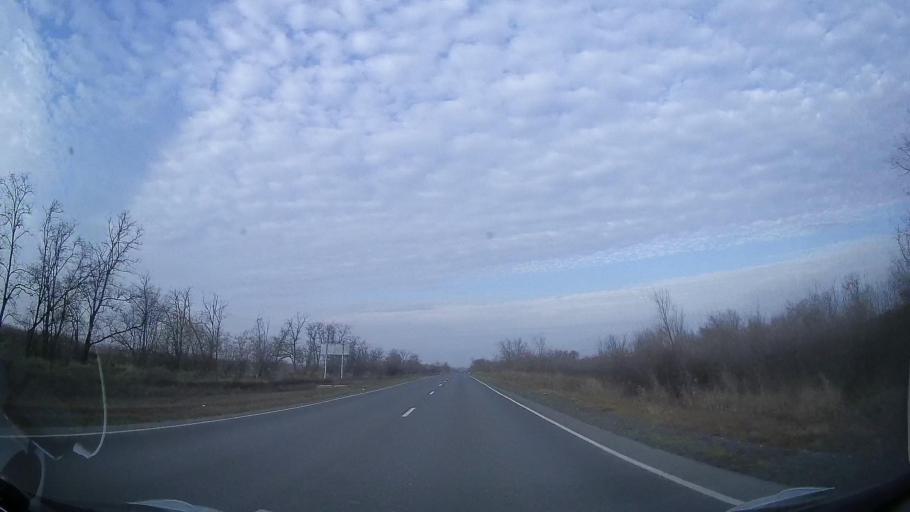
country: RU
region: Rostov
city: Bagayevskaya
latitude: 47.1552
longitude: 40.2764
